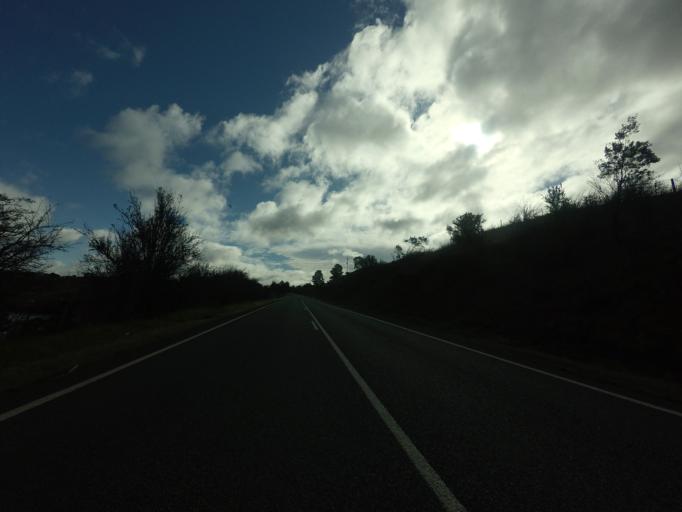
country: AU
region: Tasmania
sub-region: Derwent Valley
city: New Norfolk
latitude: -42.6852
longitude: 146.9410
